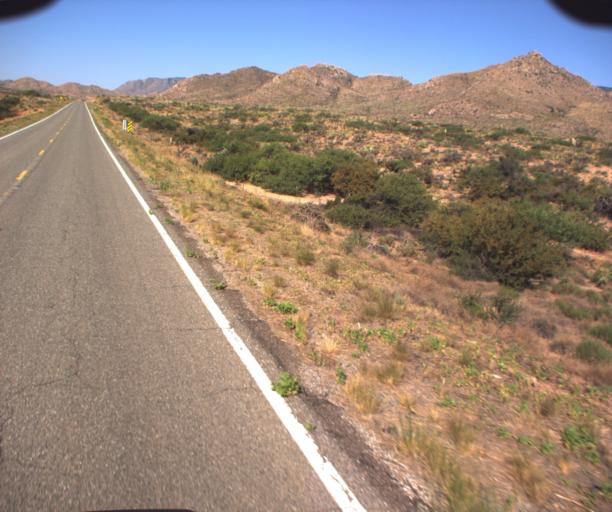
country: US
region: Arizona
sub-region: Graham County
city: Swift Trail Junction
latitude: 32.5871
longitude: -109.6995
